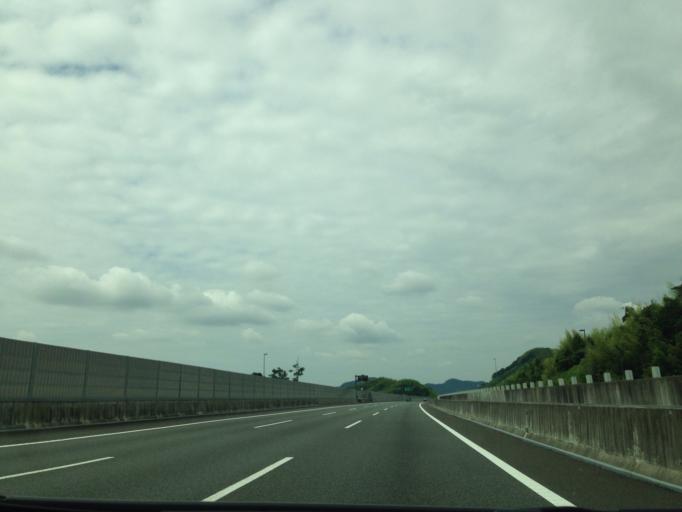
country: JP
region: Shizuoka
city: Fujieda
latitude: 34.9203
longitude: 138.2673
